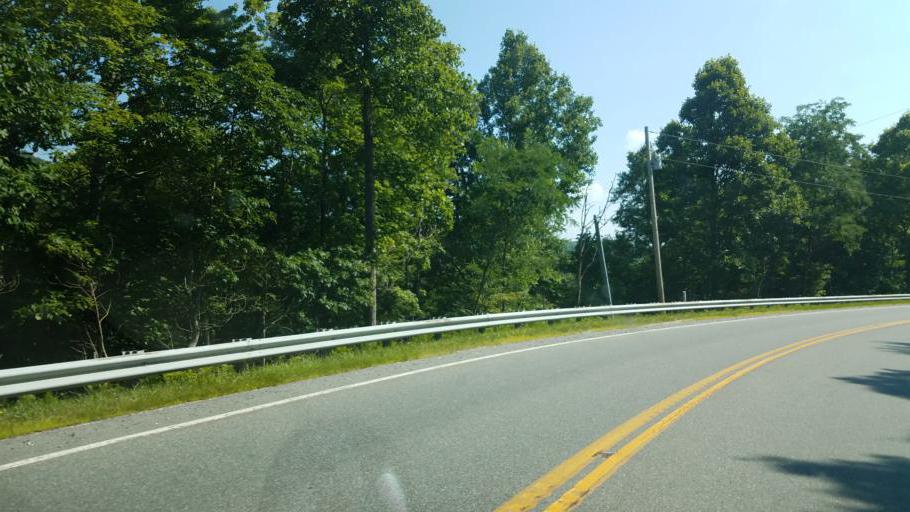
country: US
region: North Carolina
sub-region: Avery County
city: Newland
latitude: 35.9547
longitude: -81.8753
